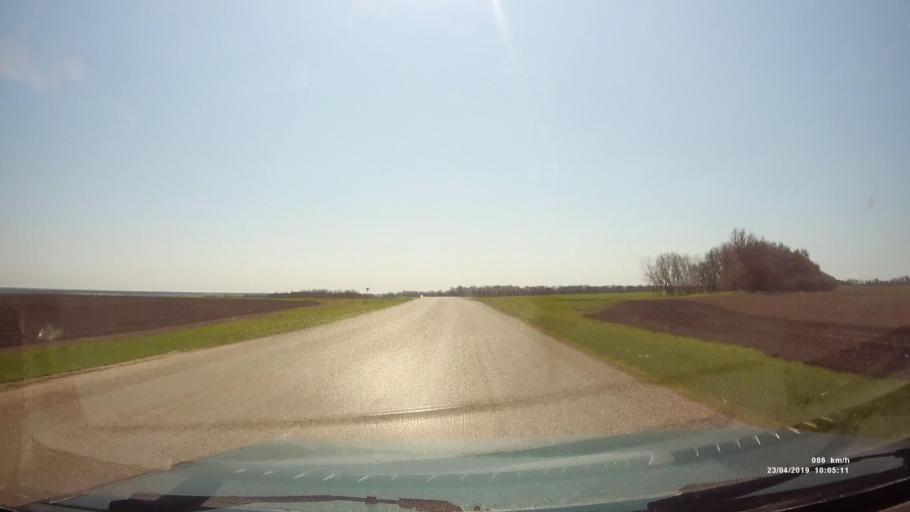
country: RU
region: Rostov
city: Sovetskoye
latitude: 46.7440
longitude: 42.2147
